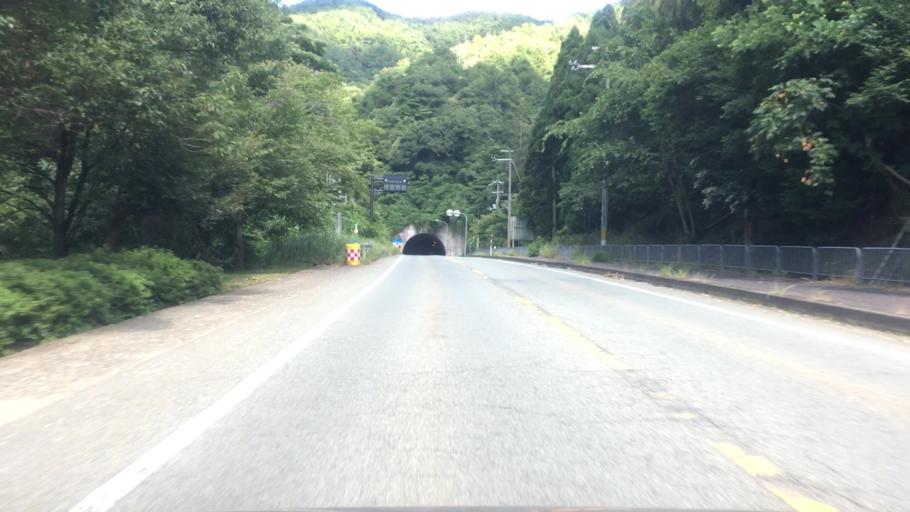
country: JP
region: Hyogo
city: Toyooka
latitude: 35.5777
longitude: 134.7519
